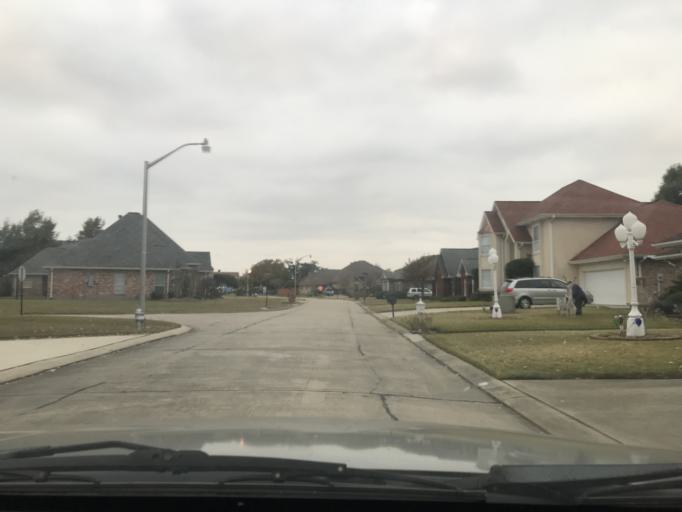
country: US
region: Louisiana
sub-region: Jefferson Parish
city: Woodmere
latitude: 29.8707
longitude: -90.0907
